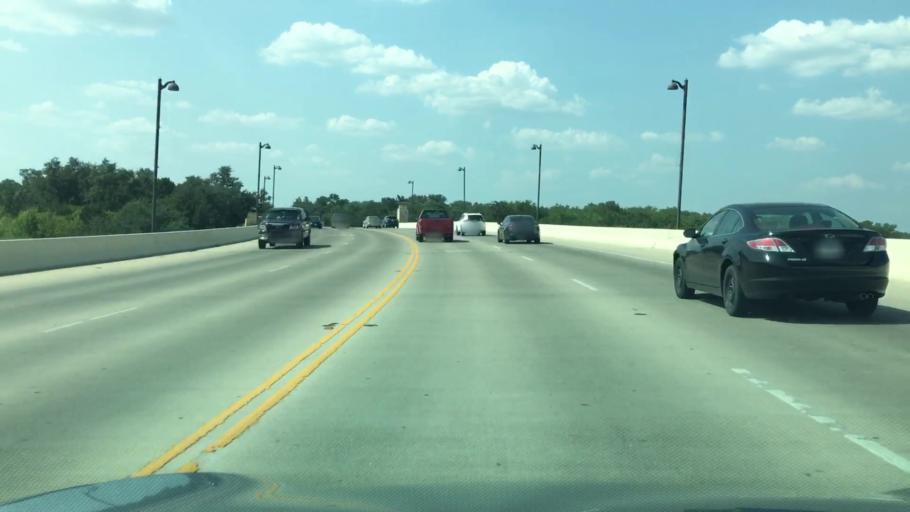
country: US
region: Texas
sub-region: Hays County
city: San Marcos
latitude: 29.8728
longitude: -97.9661
